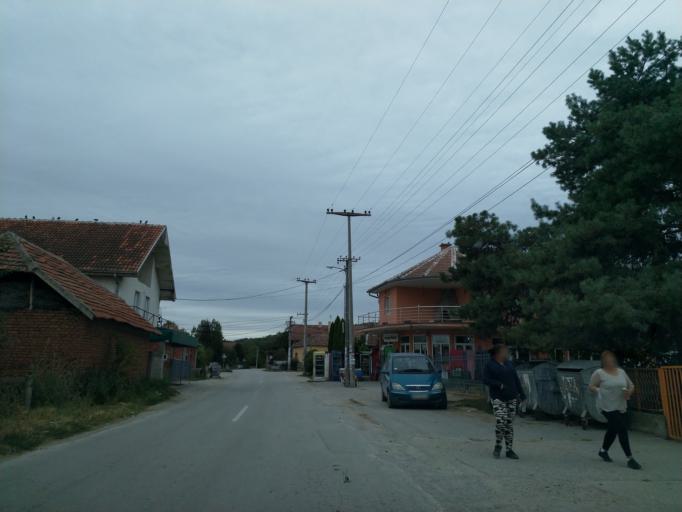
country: RS
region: Central Serbia
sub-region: Pomoravski Okrug
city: Cuprija
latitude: 43.8688
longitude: 21.3218
